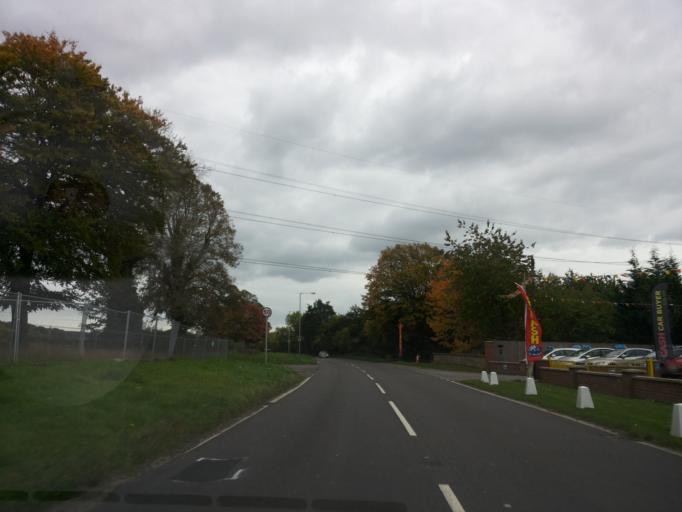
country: GB
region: England
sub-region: Buckinghamshire
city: Great Missenden
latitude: 51.6857
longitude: -0.6834
